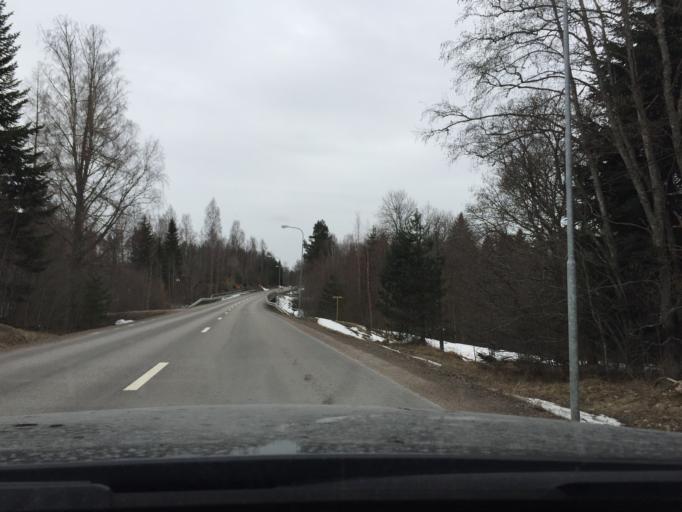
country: SE
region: Gaevleborg
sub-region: Sandvikens Kommun
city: Jarbo
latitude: 60.7590
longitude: 16.5354
